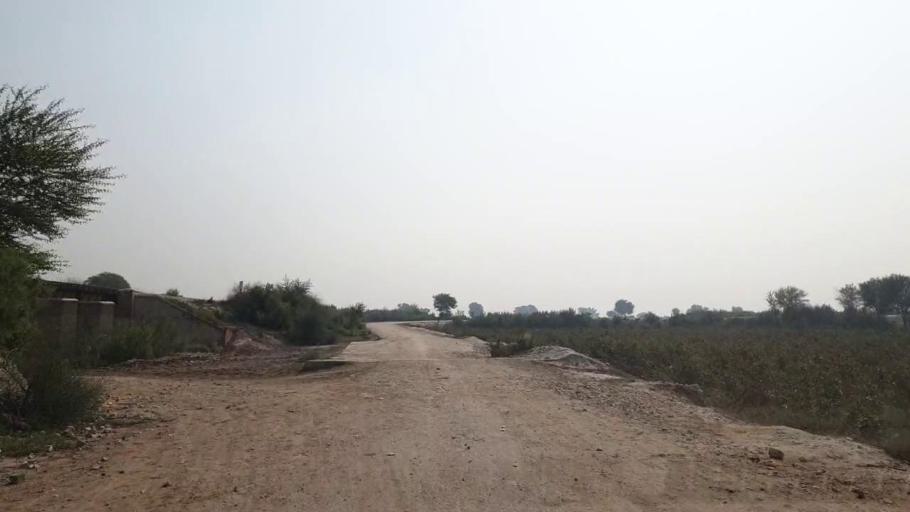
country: PK
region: Sindh
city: Bhan
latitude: 26.5162
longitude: 67.7434
